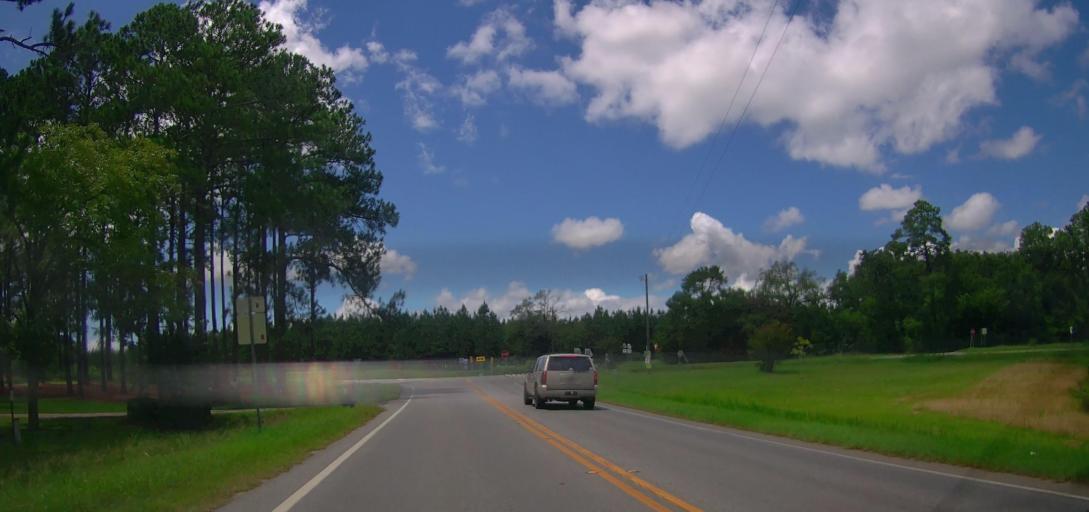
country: US
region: Georgia
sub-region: Turner County
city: Ashburn
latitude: 31.7233
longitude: -83.5828
